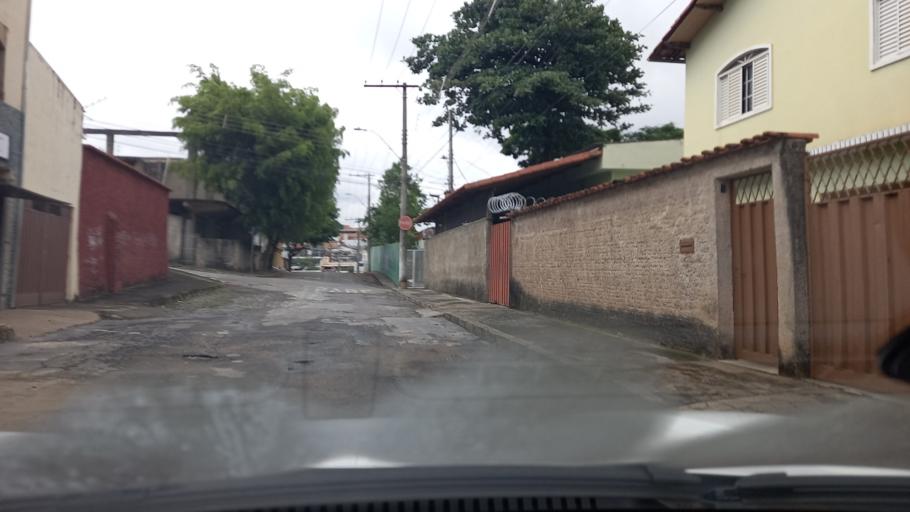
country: BR
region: Minas Gerais
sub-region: Contagem
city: Contagem
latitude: -19.9117
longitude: -43.9994
